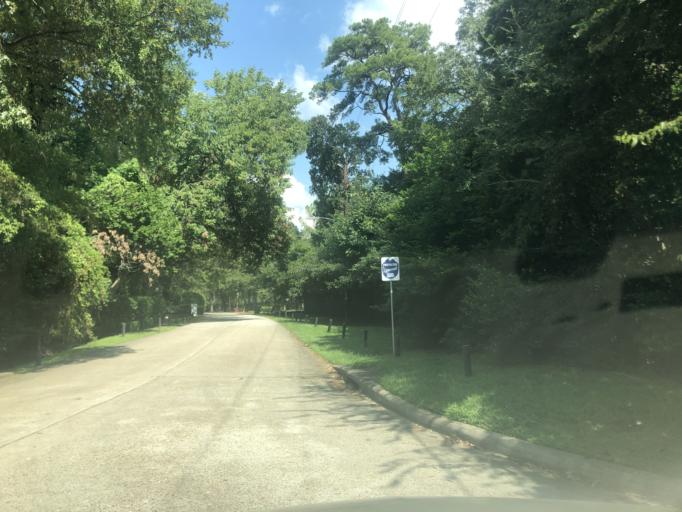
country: US
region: Texas
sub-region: Harris County
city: Bunker Hill Village
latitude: 29.7477
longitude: -95.5417
